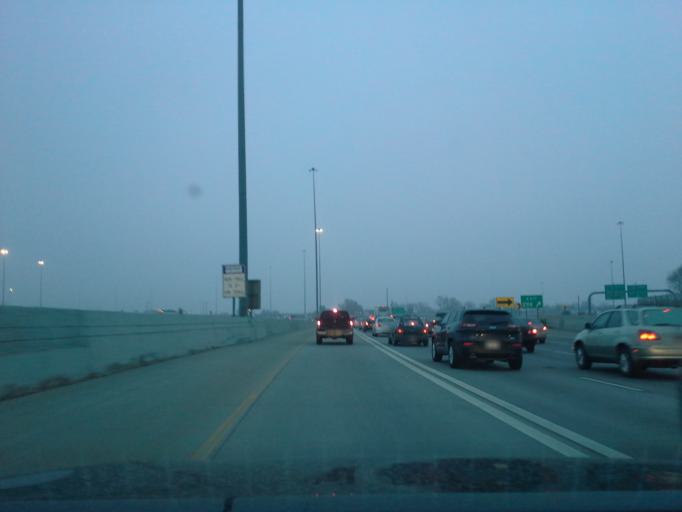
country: US
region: Utah
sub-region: Salt Lake County
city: Midvale
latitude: 40.6395
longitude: -111.9036
